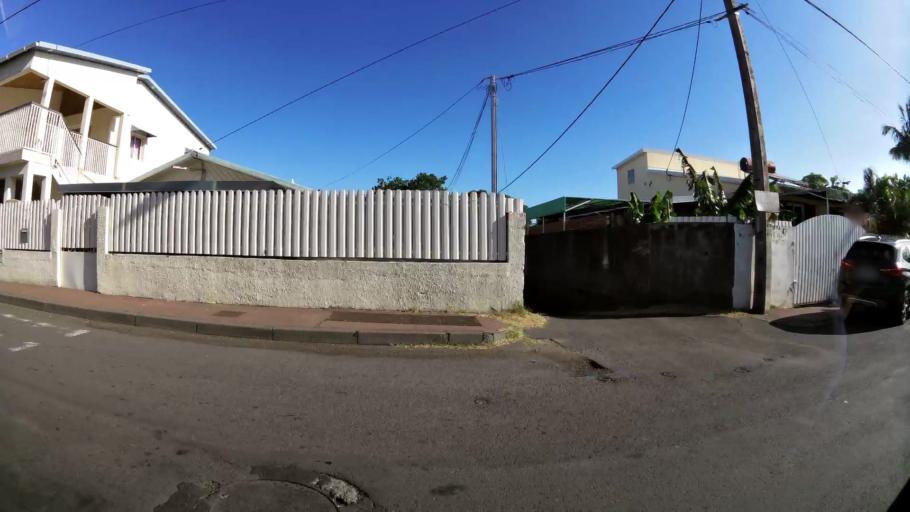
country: RE
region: Reunion
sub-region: Reunion
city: Saint-Louis
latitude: -21.2880
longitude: 55.4162
